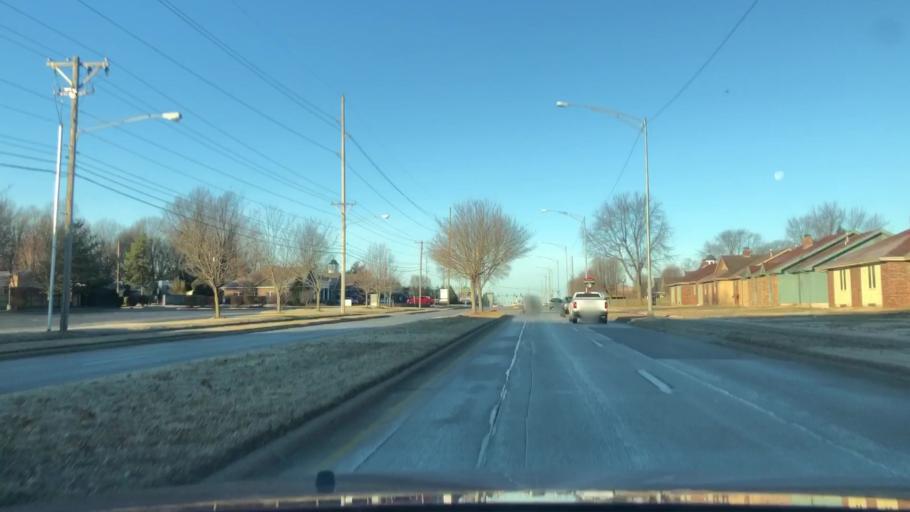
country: US
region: Missouri
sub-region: Greene County
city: Springfield
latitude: 37.1592
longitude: -93.2578
